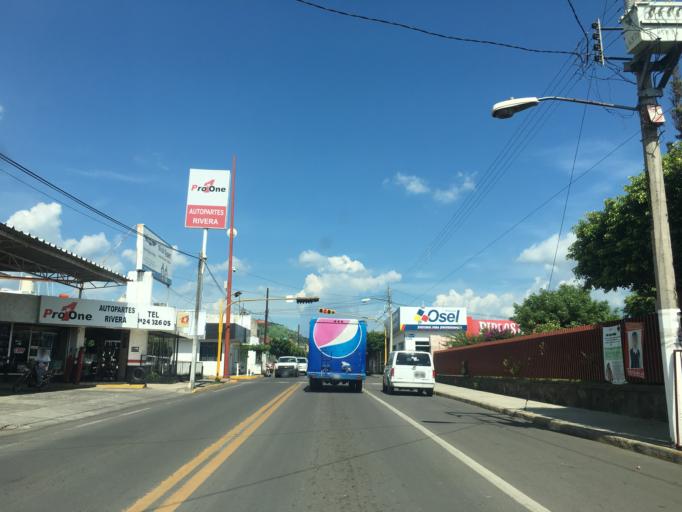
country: MX
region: Nayarit
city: Ixtlan del Rio
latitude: 21.0364
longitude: -104.3758
